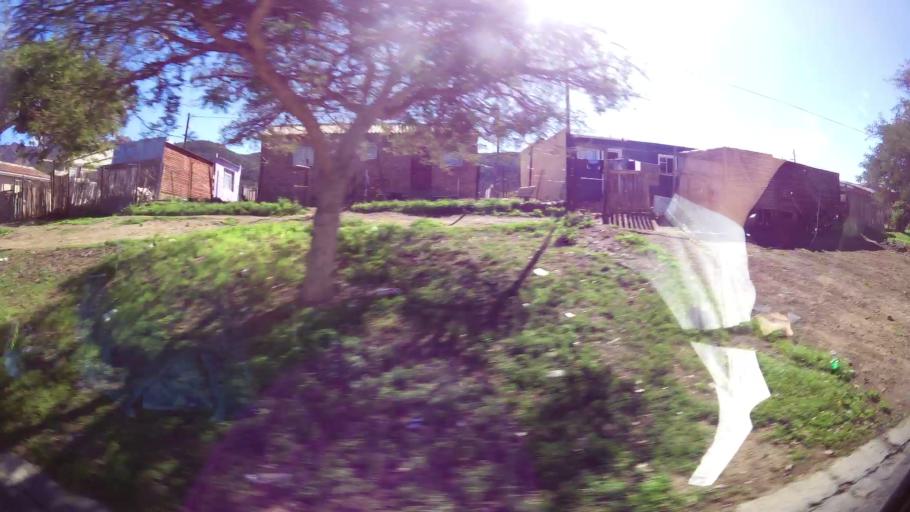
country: ZA
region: Western Cape
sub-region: Cape Winelands District Municipality
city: Ashton
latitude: -33.7821
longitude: 20.1256
